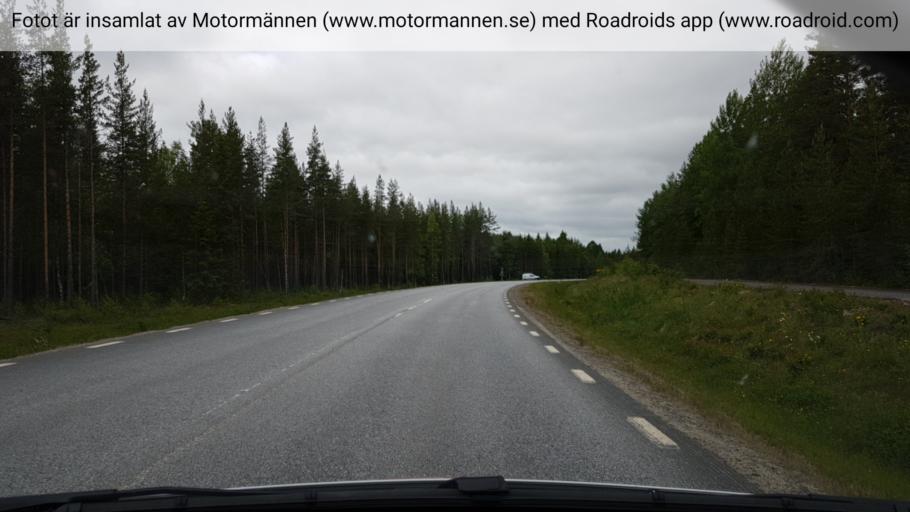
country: SE
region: Vaesterbotten
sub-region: Vannas Kommun
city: Vaennaes
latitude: 63.9471
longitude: 19.7611
